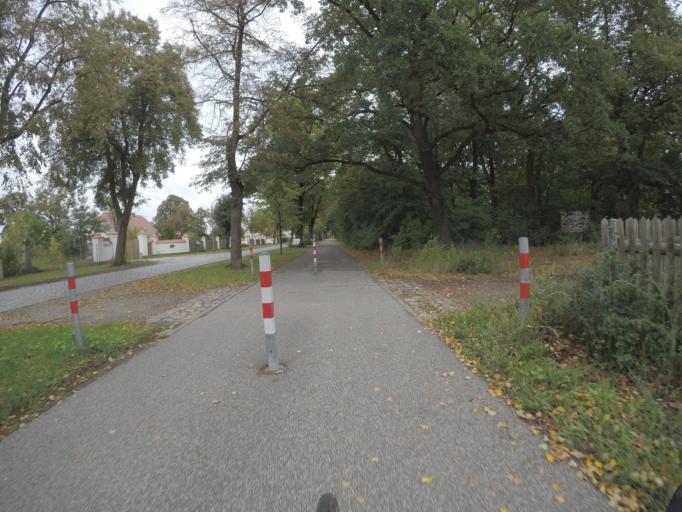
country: DE
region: Berlin
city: Buch
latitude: 52.6641
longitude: 13.4940
